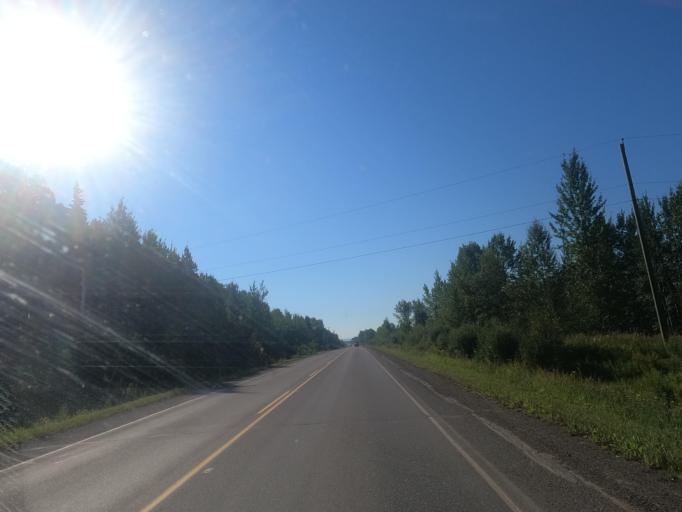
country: CA
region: British Columbia
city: Burns Lake
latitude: 54.2719
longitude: -125.8096
